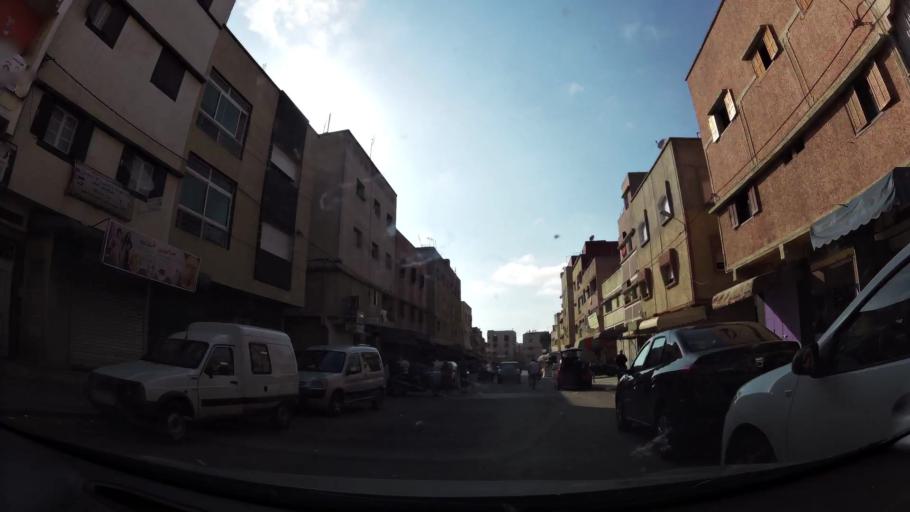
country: MA
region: Rabat-Sale-Zemmour-Zaer
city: Sale
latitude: 34.0525
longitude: -6.7796
